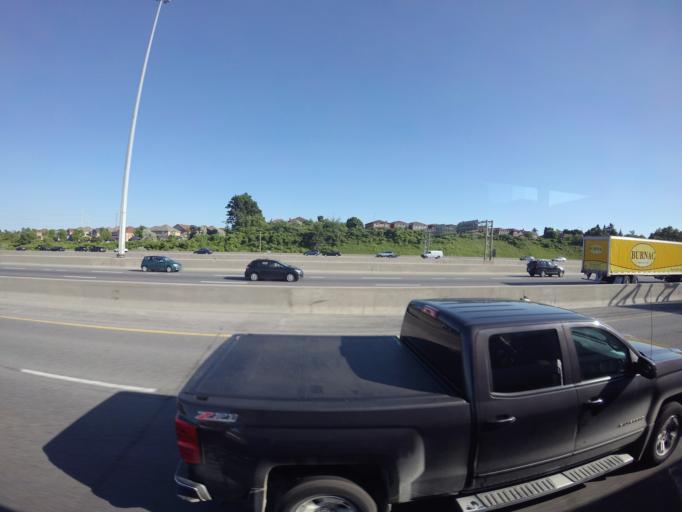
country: CA
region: Ontario
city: Scarborough
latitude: 43.7958
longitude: -79.2029
